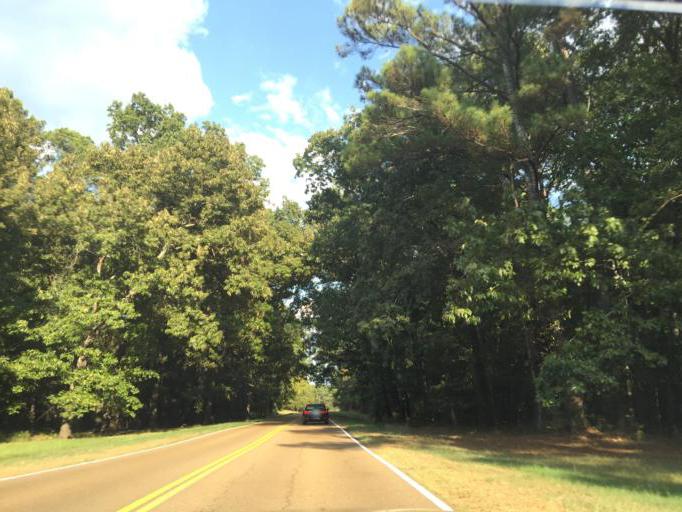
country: US
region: Mississippi
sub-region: Madison County
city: Ridgeland
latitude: 32.4272
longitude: -90.1191
